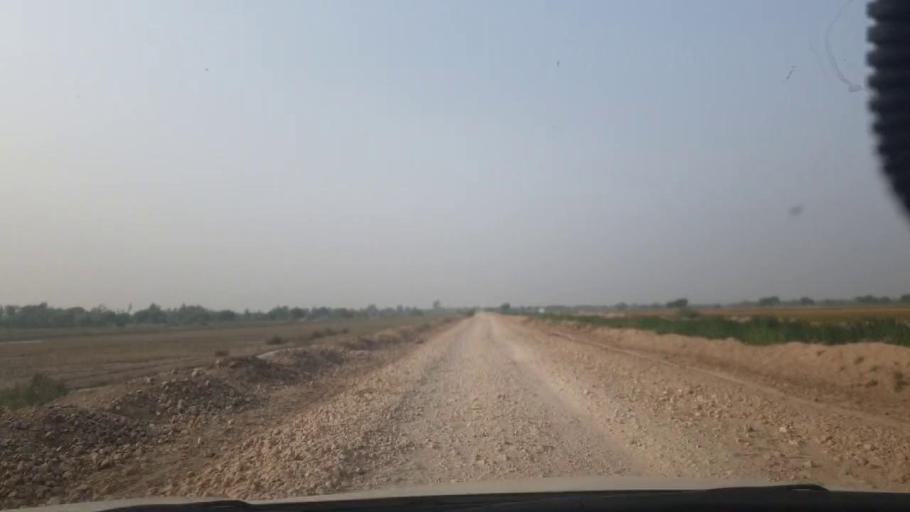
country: PK
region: Sindh
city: Bulri
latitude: 24.7916
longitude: 68.4182
